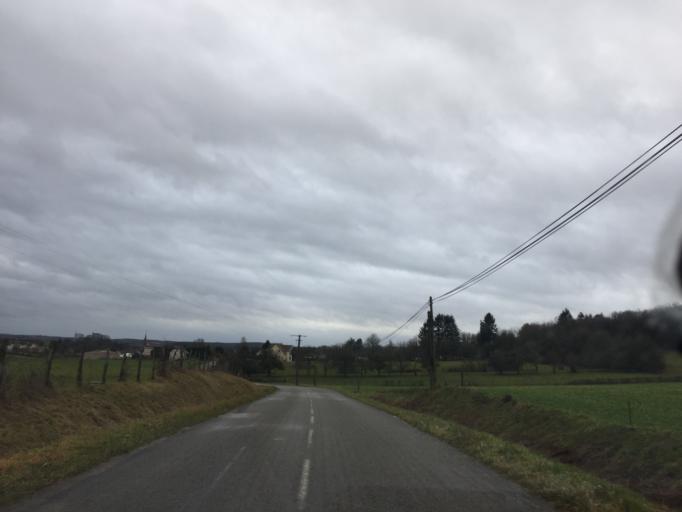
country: FR
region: Franche-Comte
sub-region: Departement du Jura
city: Orchamps
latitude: 47.1714
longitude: 5.5694
